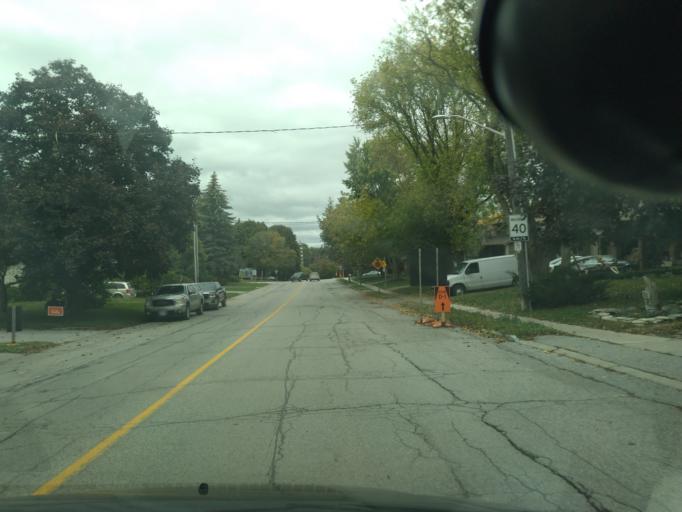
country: CA
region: Ontario
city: Newmarket
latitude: 44.0537
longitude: -79.4648
